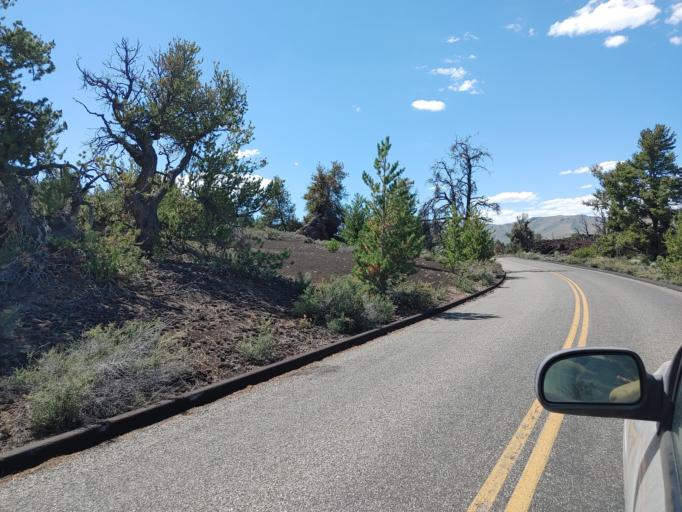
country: US
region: Idaho
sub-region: Butte County
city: Arco
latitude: 43.4529
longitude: -113.5440
